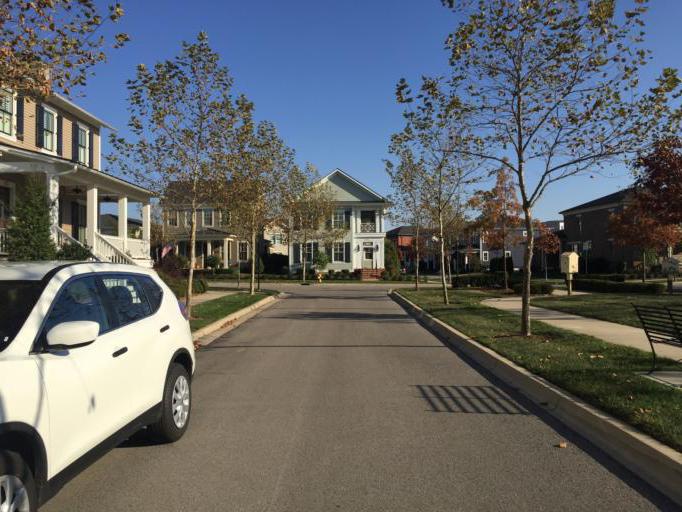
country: US
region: Kentucky
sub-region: Jefferson County
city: Worthington
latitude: 38.3264
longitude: -85.5691
